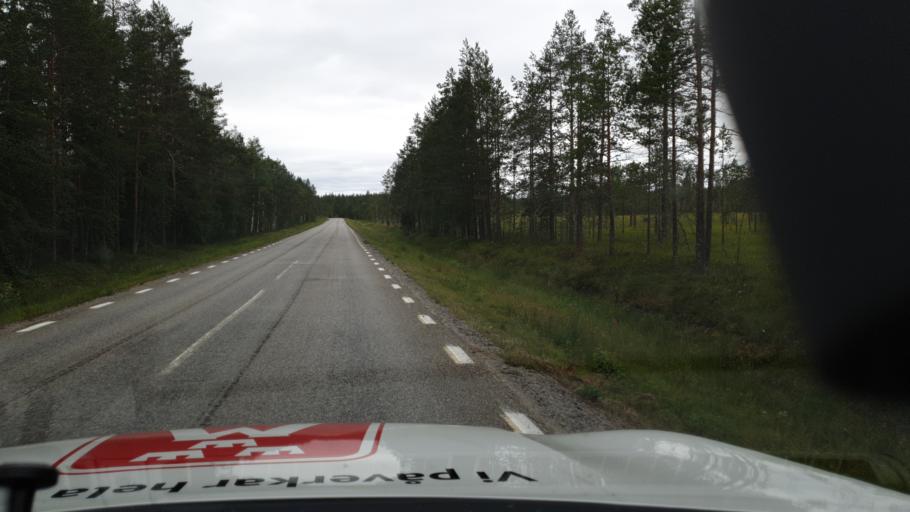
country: SE
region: Vaesterbotten
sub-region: Umea Kommun
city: Saevar
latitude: 64.0982
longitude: 20.5202
